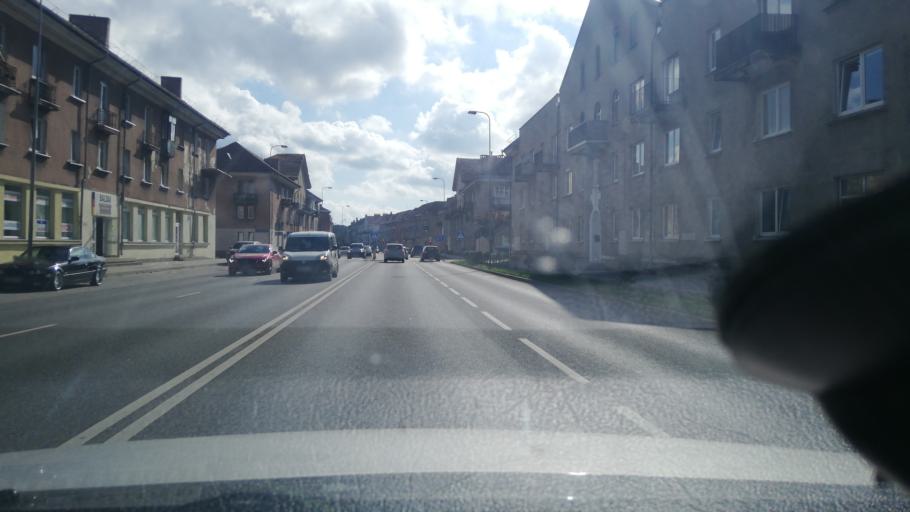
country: LT
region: Klaipedos apskritis
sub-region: Klaipeda
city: Klaipeda
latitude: 55.6799
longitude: 21.1517
